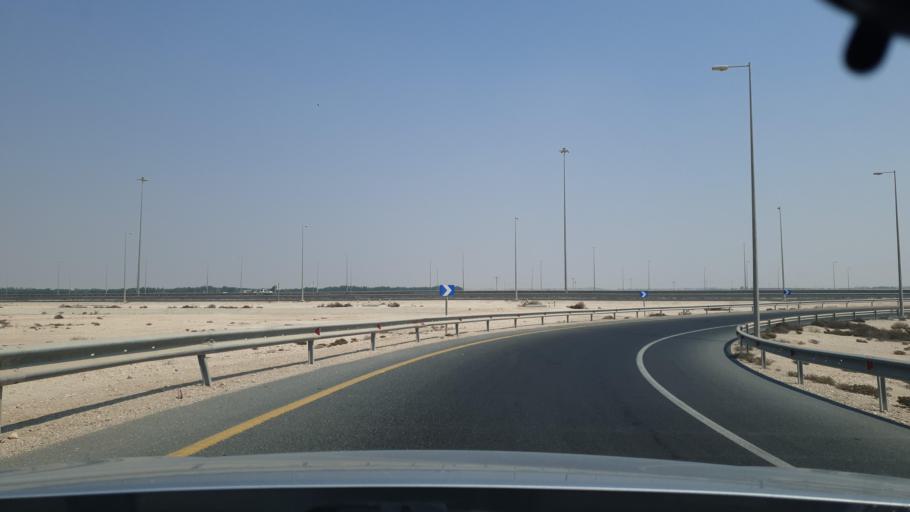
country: QA
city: Al Ghuwayriyah
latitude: 25.8311
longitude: 51.3485
